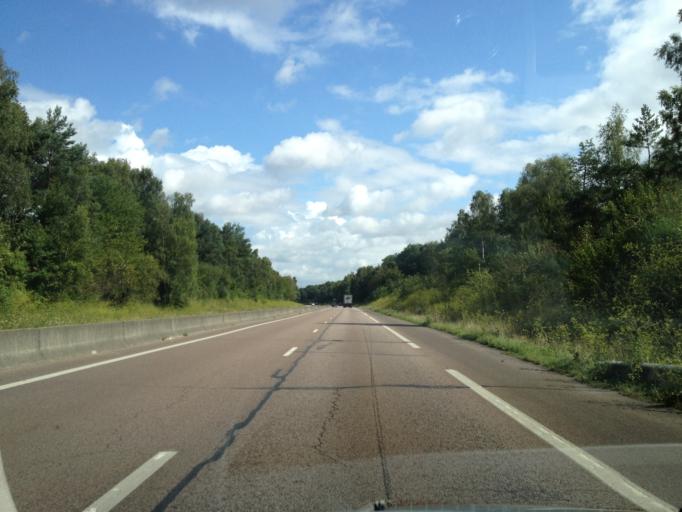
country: FR
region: Haute-Normandie
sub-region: Departement de la Seine-Maritime
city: Oissel
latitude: 49.3548
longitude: 1.0828
